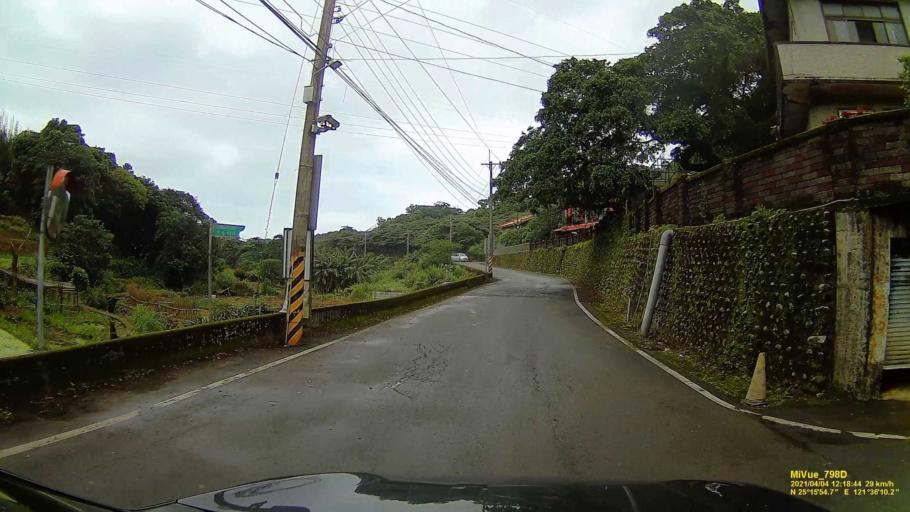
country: TW
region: Taiwan
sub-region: Keelung
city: Keelung
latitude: 25.2654
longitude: 121.6029
